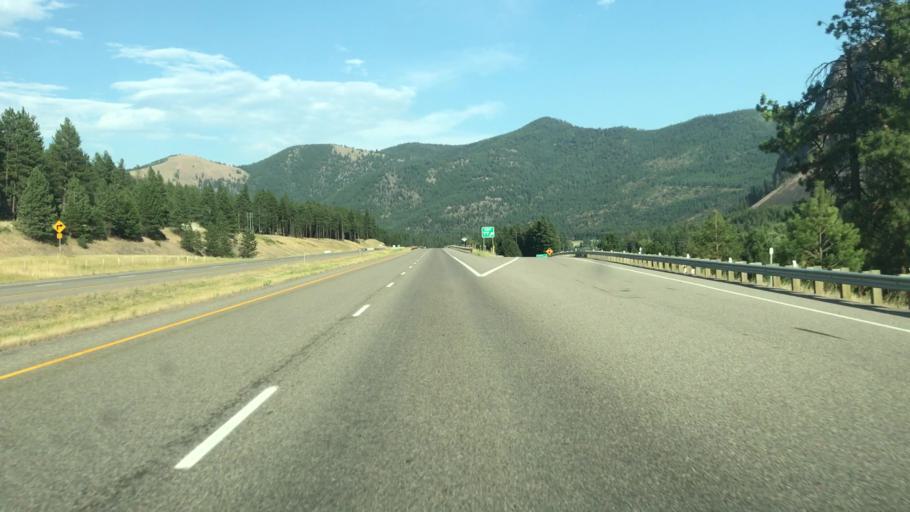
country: US
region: Montana
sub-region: Missoula County
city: Frenchtown
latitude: 46.9944
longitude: -114.4504
